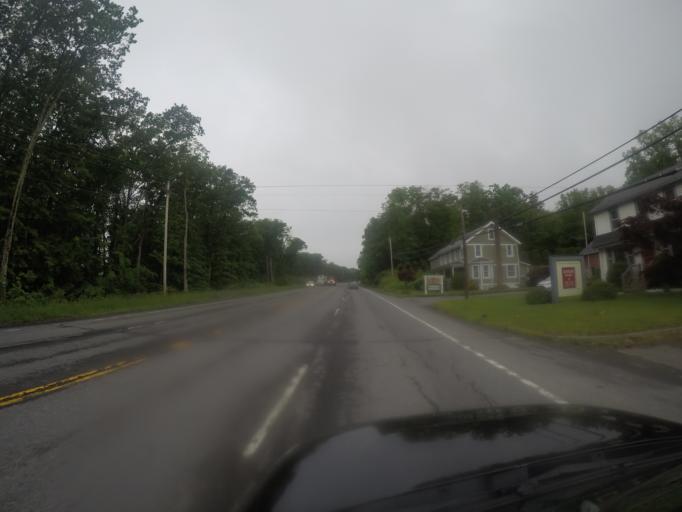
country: US
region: New York
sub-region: Ulster County
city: West Hurley
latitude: 41.9958
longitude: -74.0931
